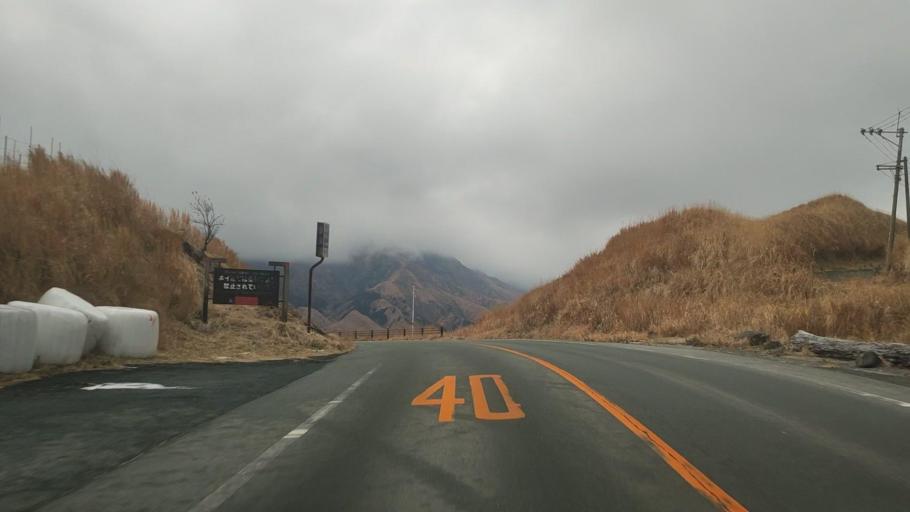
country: JP
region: Kumamoto
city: Aso
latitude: 32.9067
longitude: 131.1549
